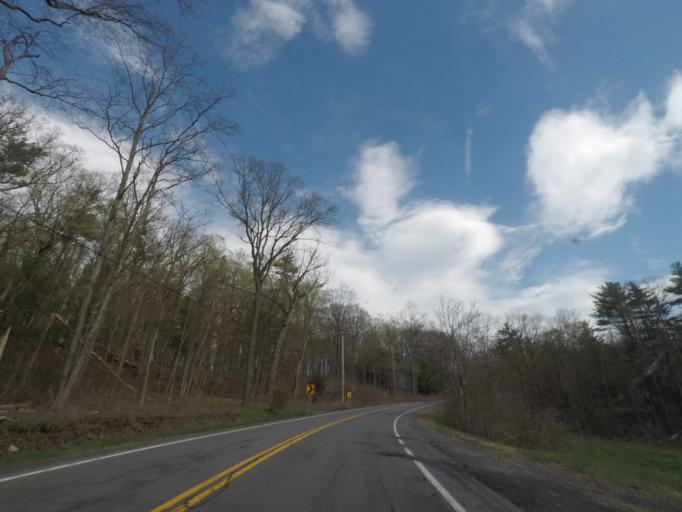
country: US
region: New York
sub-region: Albany County
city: Voorheesville
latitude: 42.5720
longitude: -73.9151
